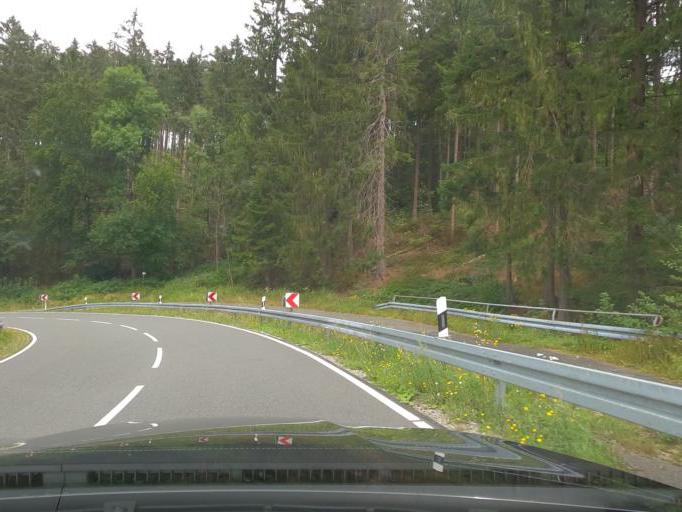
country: DE
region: Lower Saxony
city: Wildemann
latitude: 51.8604
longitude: 10.3197
